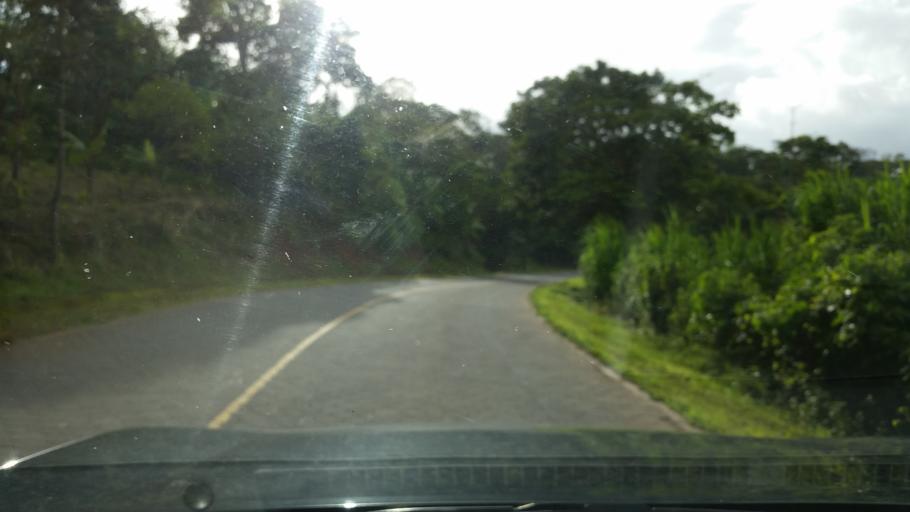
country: NI
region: Matagalpa
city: San Ramon
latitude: 13.1736
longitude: -85.7288
